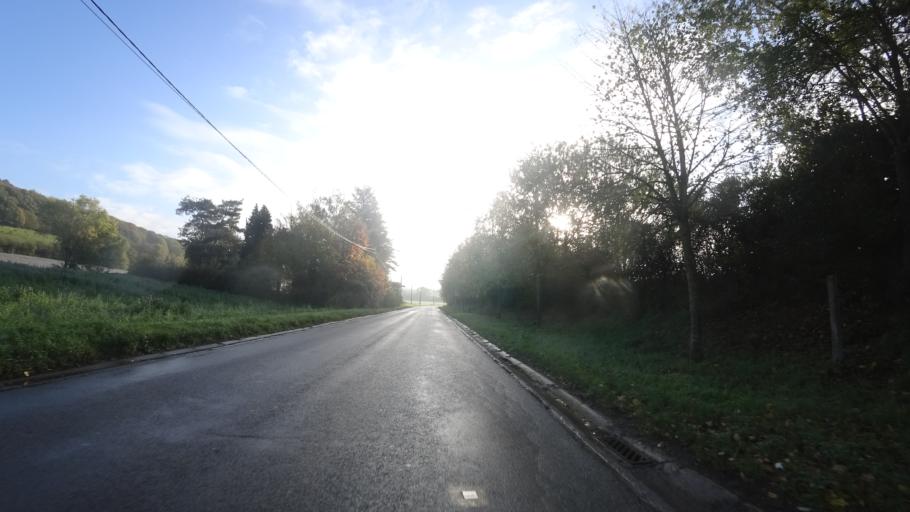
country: BE
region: Wallonia
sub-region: Province de Namur
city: Floreffe
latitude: 50.4498
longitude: 4.7728
